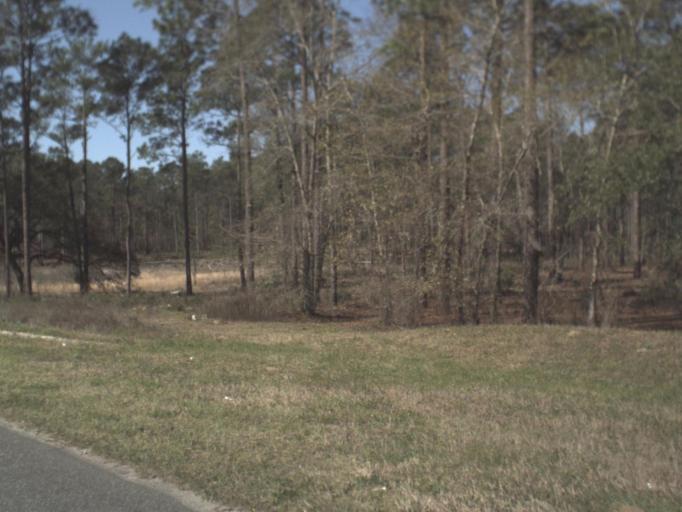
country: US
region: Florida
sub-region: Leon County
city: Woodville
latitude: 30.3532
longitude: -84.3072
